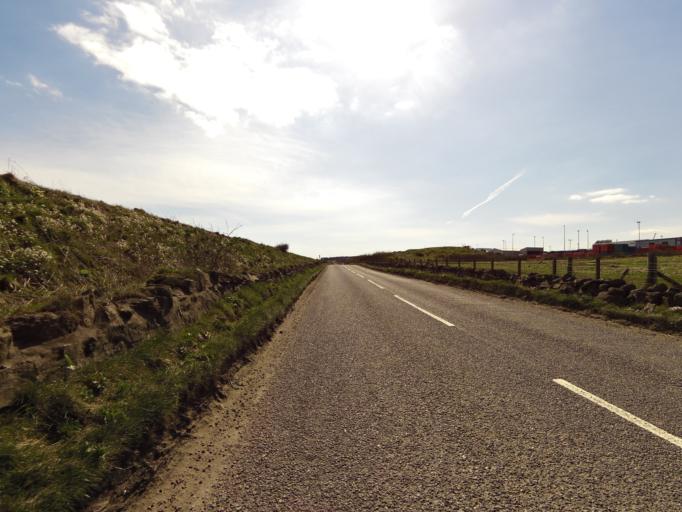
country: GB
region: Scotland
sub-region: Aberdeen City
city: Aberdeen
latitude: 57.1190
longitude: -2.0605
